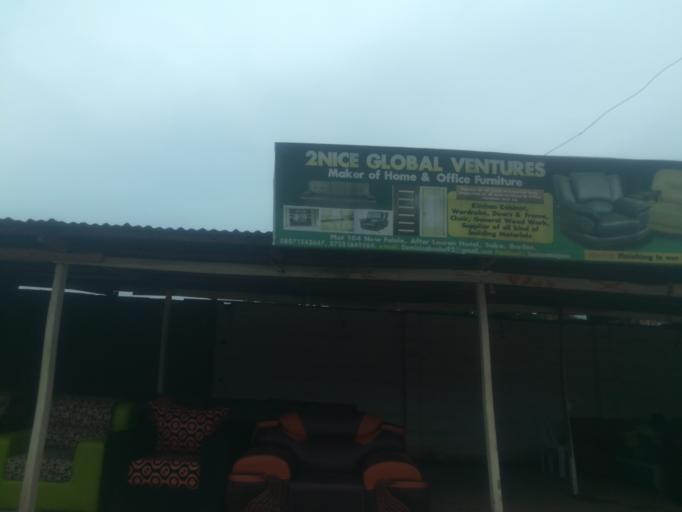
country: NG
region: Oyo
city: Ibadan
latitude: 7.3281
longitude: 3.8911
